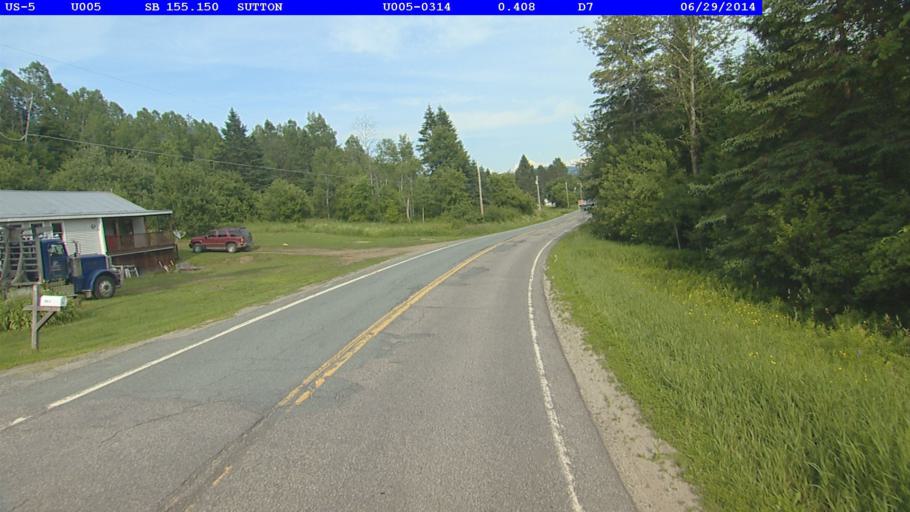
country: US
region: Vermont
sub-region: Caledonia County
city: Lyndonville
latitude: 44.6436
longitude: -71.9922
